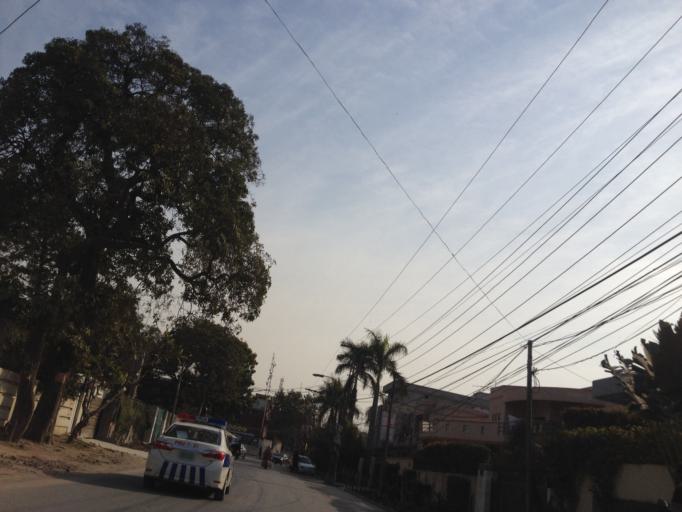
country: PK
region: Punjab
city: Lahore
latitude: 31.5049
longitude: 74.3188
